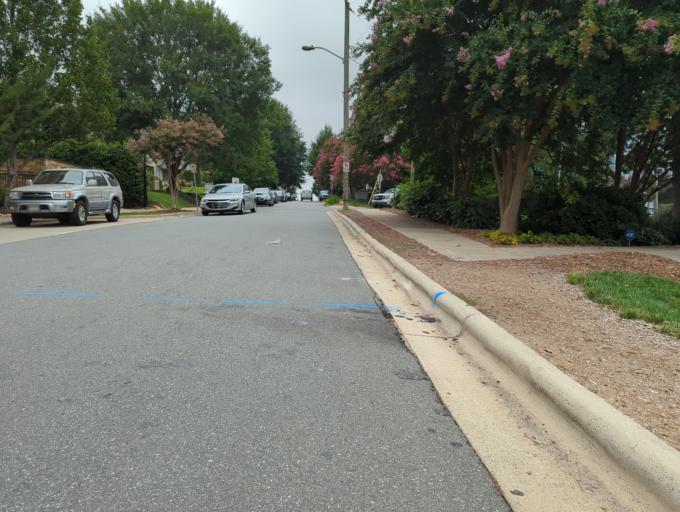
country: US
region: North Carolina
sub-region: Mecklenburg County
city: Charlotte
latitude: 35.2075
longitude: -80.8371
